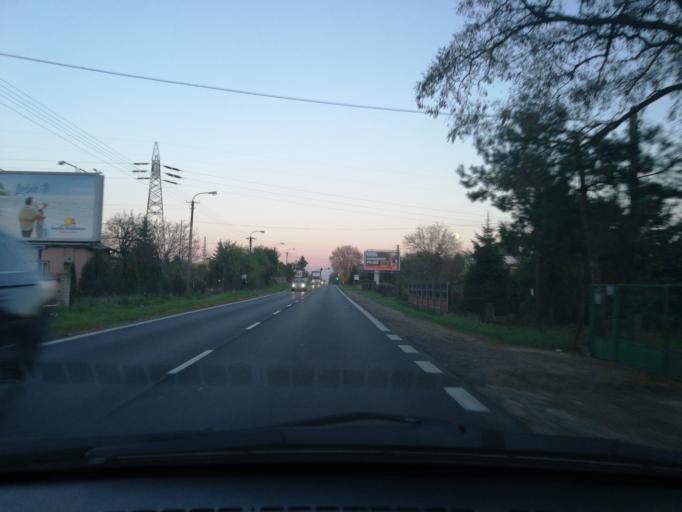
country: PL
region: Lodz Voivodeship
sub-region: Powiat lodzki wschodni
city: Andrespol
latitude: 51.7956
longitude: 19.5615
